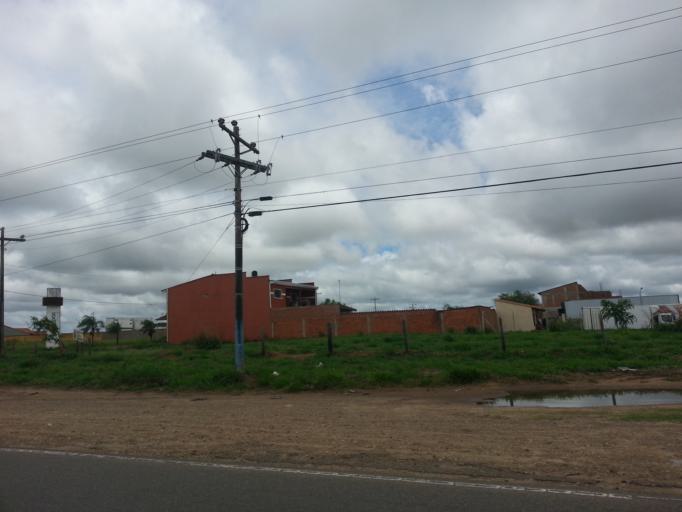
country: BO
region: Santa Cruz
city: La Belgica
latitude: -17.6351
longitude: -63.1581
